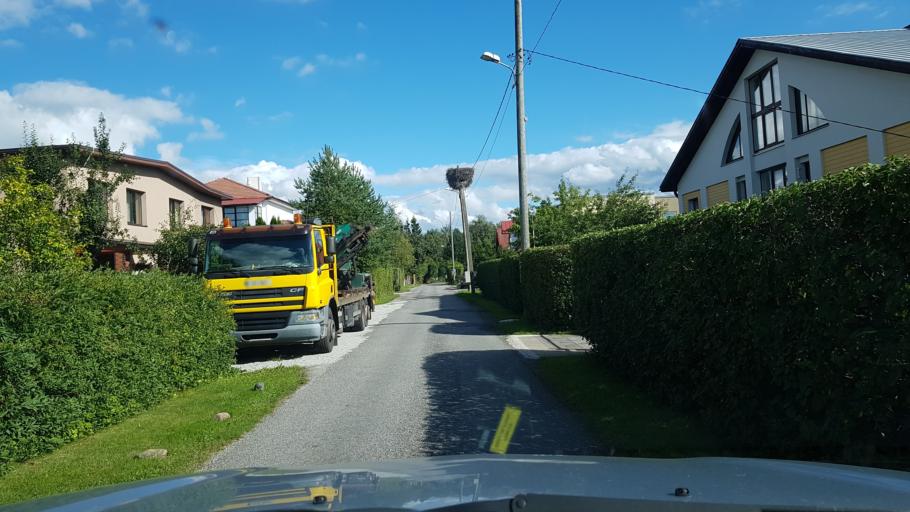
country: EE
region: Harju
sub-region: Rae vald
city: Jueri
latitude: 59.3728
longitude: 24.8446
